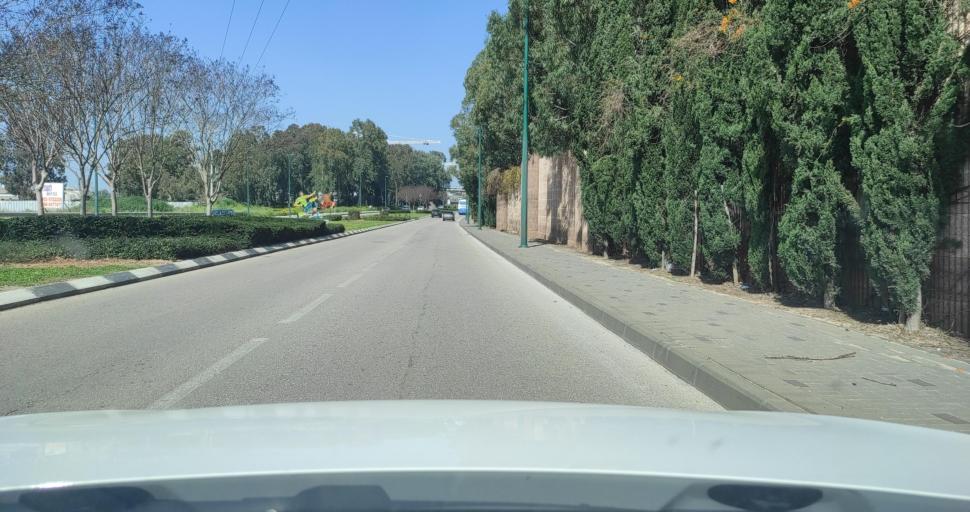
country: IL
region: Central District
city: Bet Yizhaq
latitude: 32.3122
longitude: 34.8771
